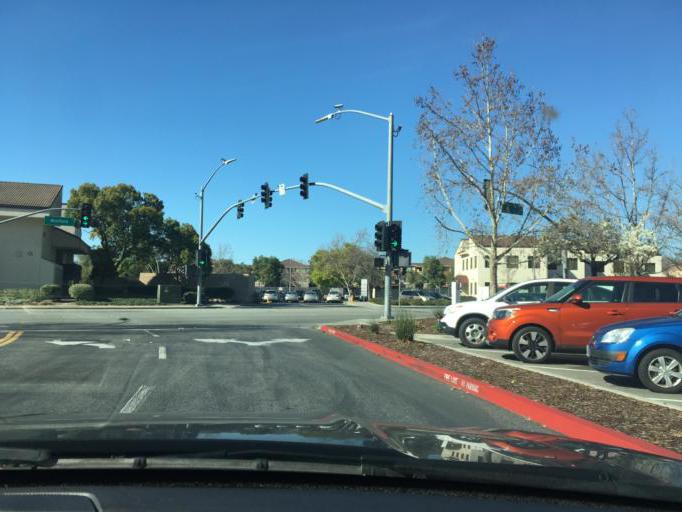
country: US
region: California
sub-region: Santa Clara County
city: Seven Trees
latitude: 37.2519
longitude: -121.8661
